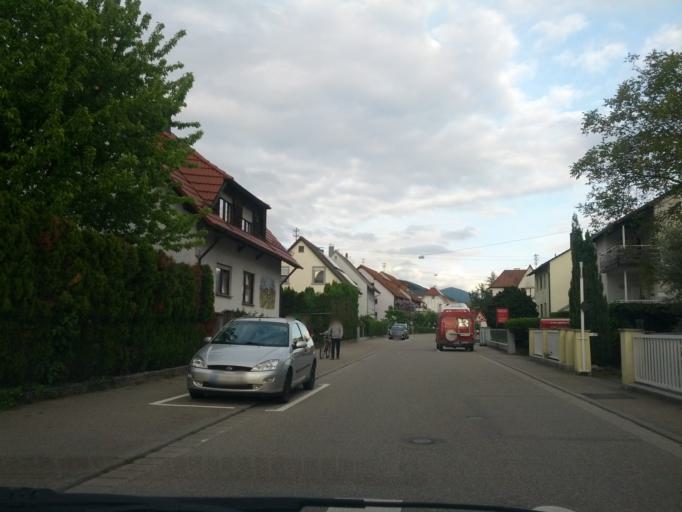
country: DE
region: Baden-Wuerttemberg
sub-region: Freiburg Region
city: Denzlingen
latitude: 48.0691
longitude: 7.8890
